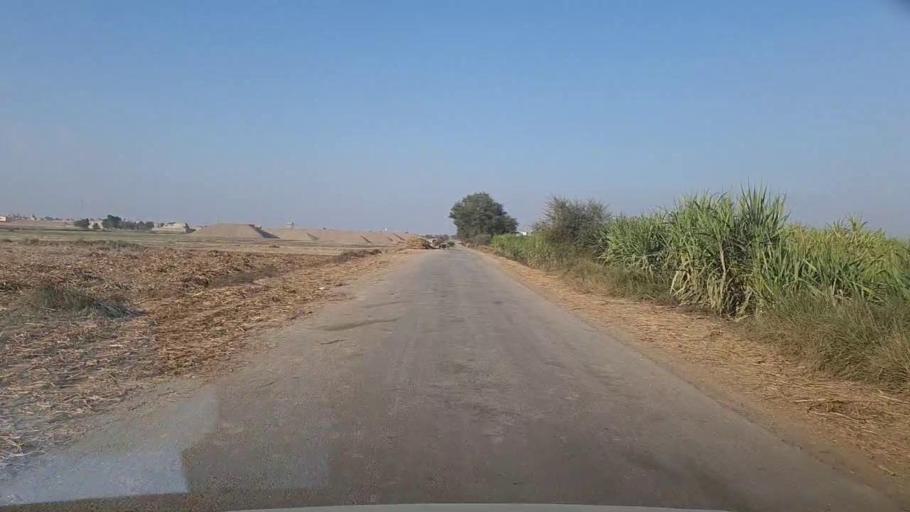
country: PK
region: Sindh
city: Phulji
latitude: 26.8532
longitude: 67.7937
